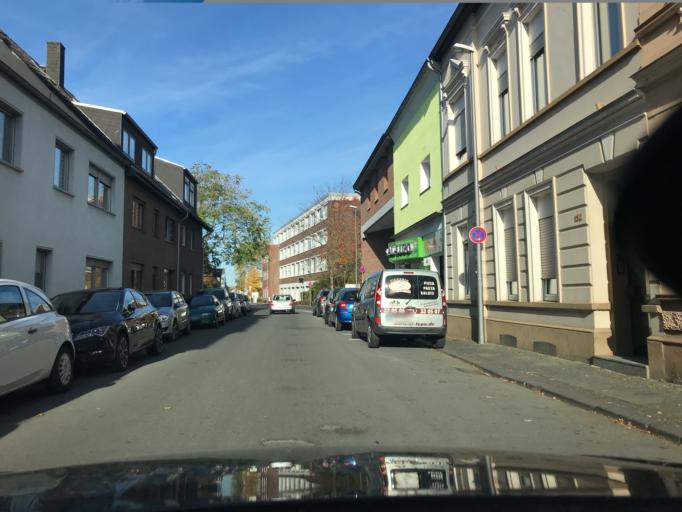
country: DE
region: North Rhine-Westphalia
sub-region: Regierungsbezirk Dusseldorf
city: Krefeld
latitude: 51.3230
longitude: 6.5849
